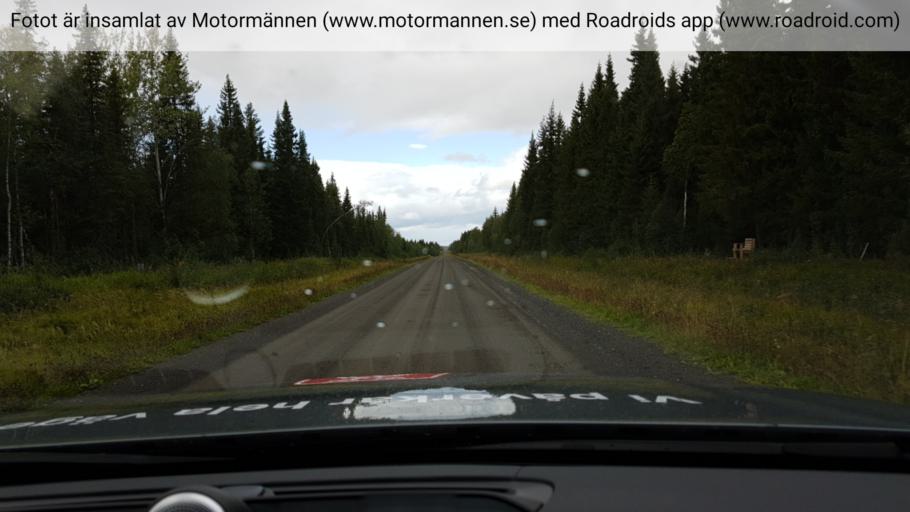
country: SE
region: Jaemtland
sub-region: OEstersunds Kommun
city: Lit
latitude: 63.6638
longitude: 14.9047
